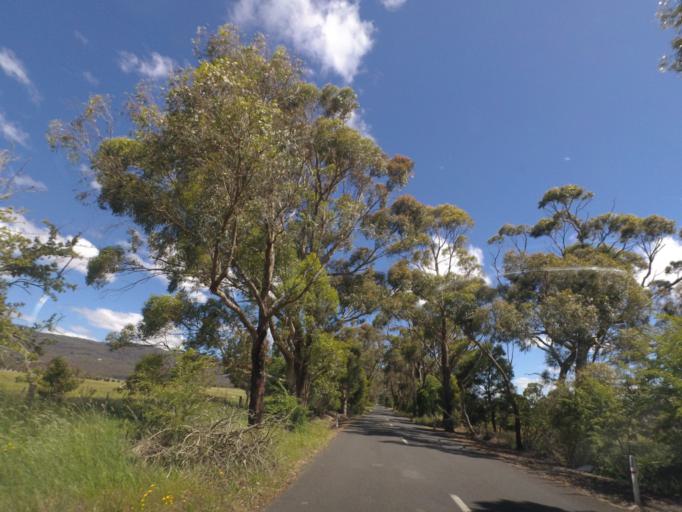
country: AU
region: Victoria
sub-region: Hume
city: Sunbury
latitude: -37.3412
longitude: 144.5571
